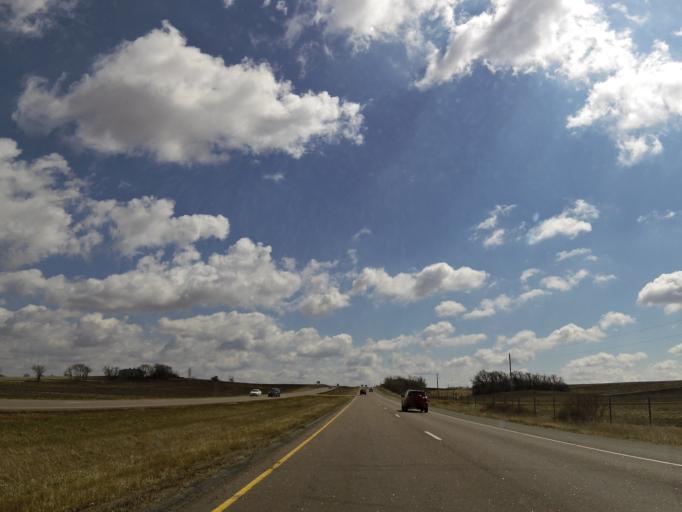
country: US
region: Minnesota
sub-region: Dakota County
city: Farmington
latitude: 44.6555
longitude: -93.0037
